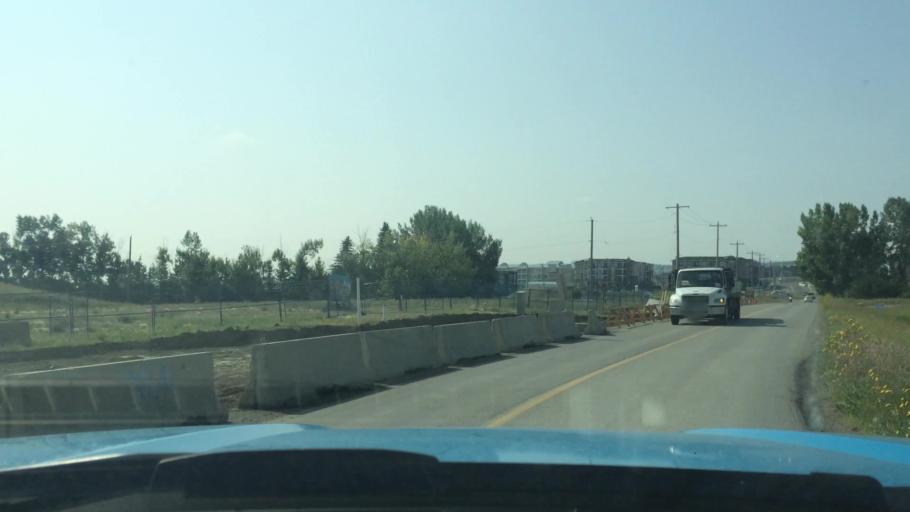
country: CA
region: Alberta
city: Calgary
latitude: 51.1758
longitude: -114.1412
